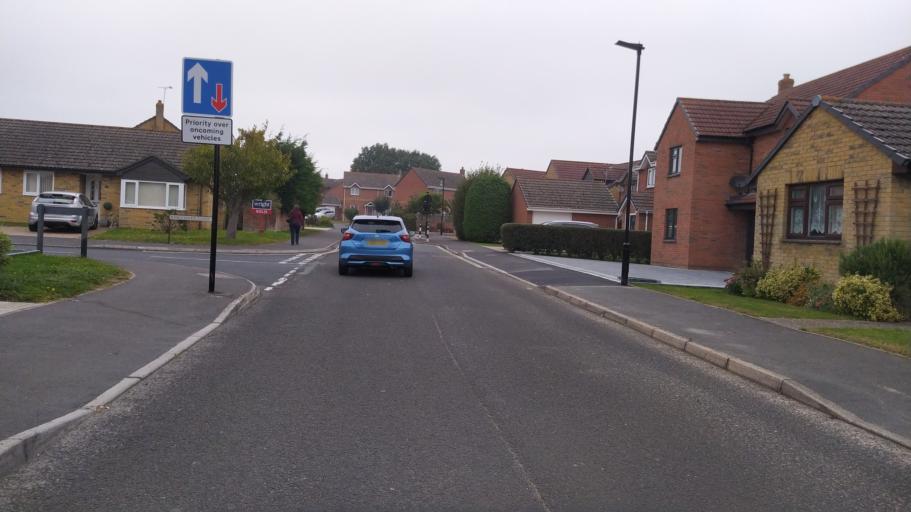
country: GB
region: England
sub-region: Isle of Wight
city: Newport
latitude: 50.6945
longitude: -1.3157
